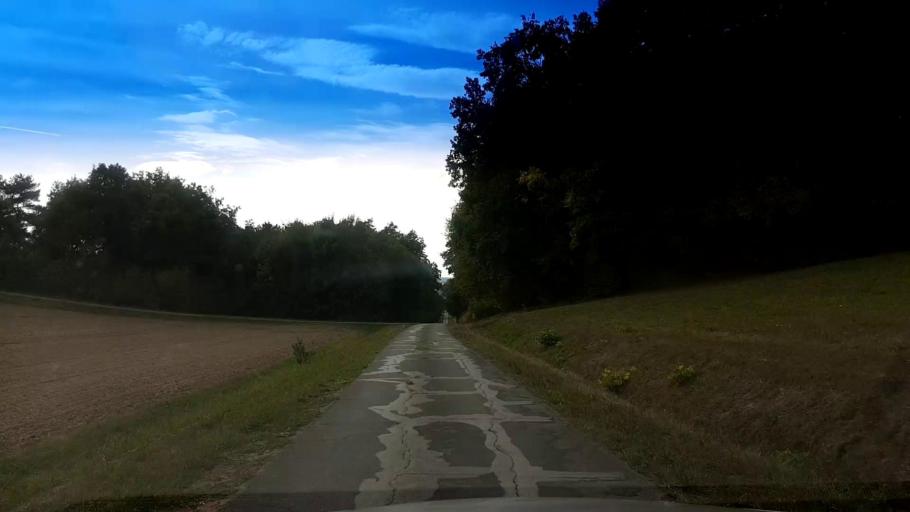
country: DE
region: Bavaria
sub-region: Upper Franconia
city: Lauter
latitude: 49.9537
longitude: 10.7688
